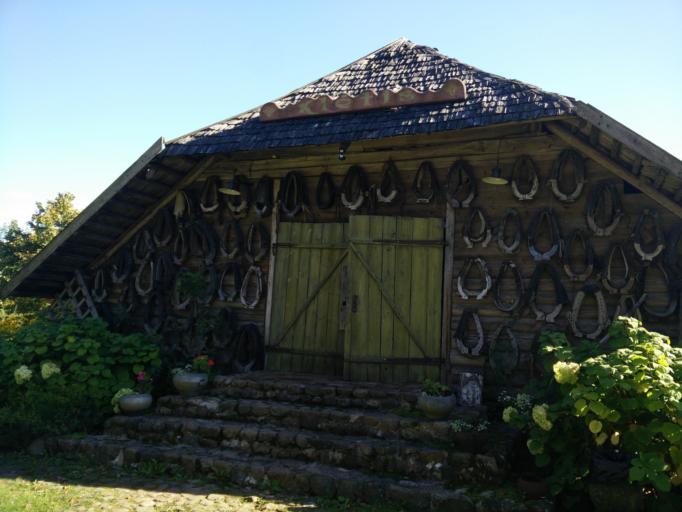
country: LT
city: Svencioneliai
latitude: 55.2691
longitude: 25.7725
